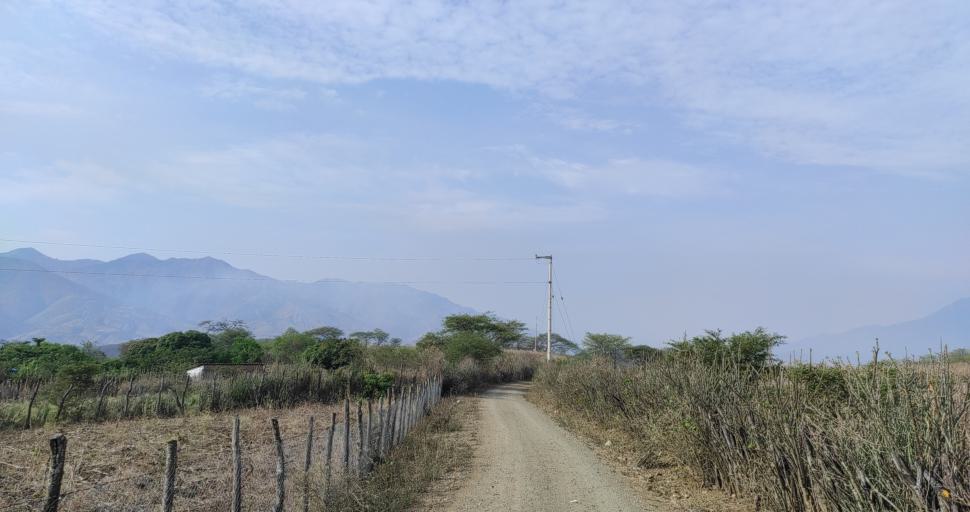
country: EC
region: Loja
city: Catacocha
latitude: -4.0079
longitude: -79.6978
